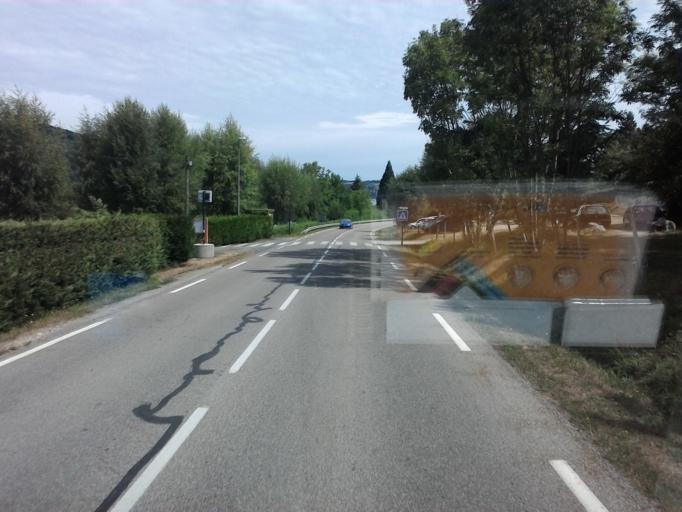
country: FR
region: Rhone-Alpes
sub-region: Departement de l'Isere
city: Bilieu
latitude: 45.4458
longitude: 5.5314
